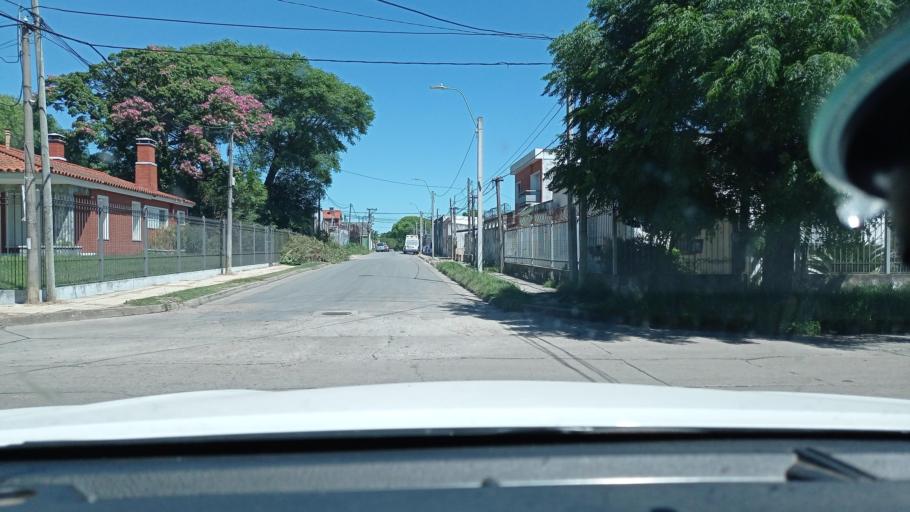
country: UY
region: Canelones
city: Las Piedras
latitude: -34.7281
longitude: -56.2248
